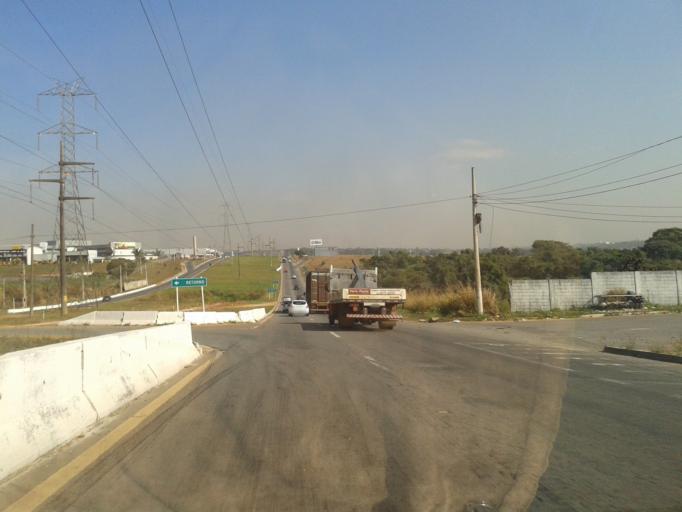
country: BR
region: Goias
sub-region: Aparecida De Goiania
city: Aparecida de Goiania
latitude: -16.7866
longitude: -49.2454
